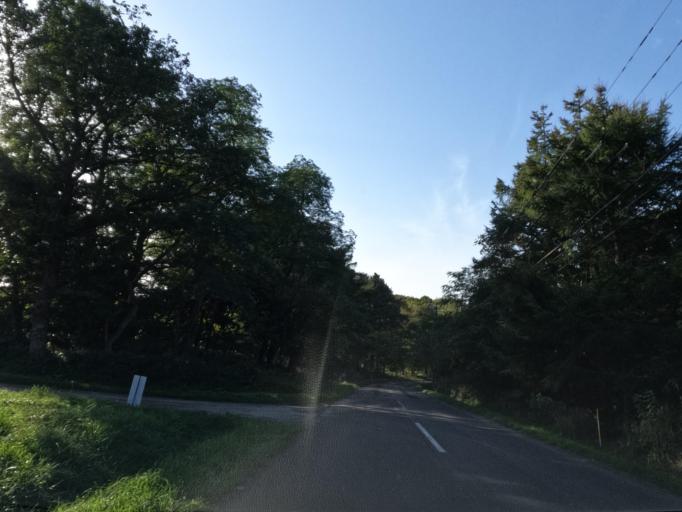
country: JP
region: Hokkaido
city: Date
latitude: 42.3973
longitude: 140.9339
